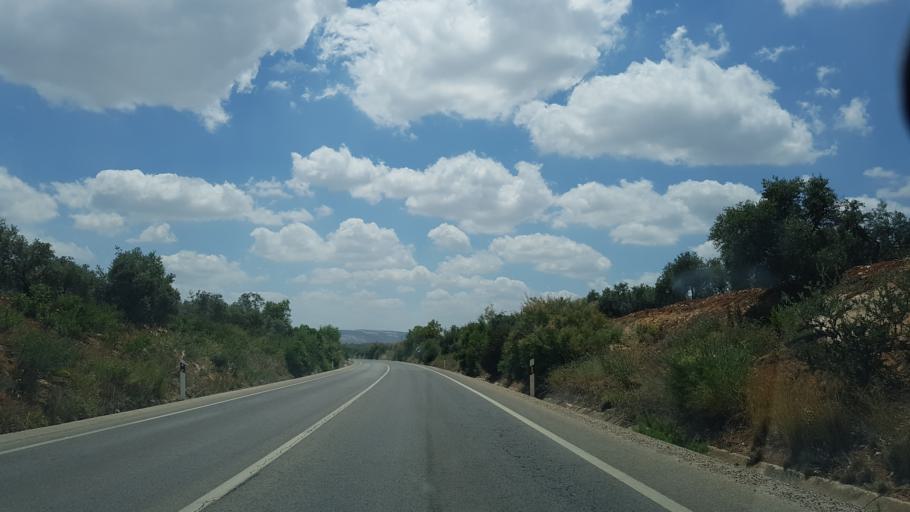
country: ES
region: Andalusia
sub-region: Province of Cordoba
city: Cabra
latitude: 37.5144
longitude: -4.4451
